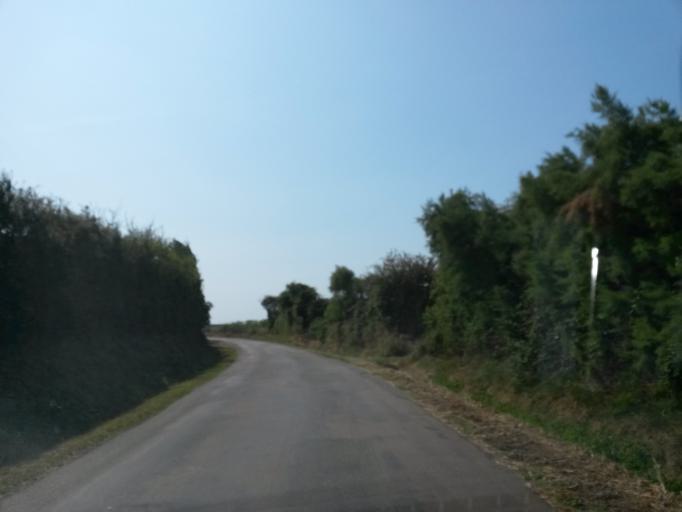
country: FR
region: Pays de la Loire
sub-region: Departement de la Vendee
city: Saint-Hilaire-de-Talmont
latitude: 46.4383
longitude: -1.6032
